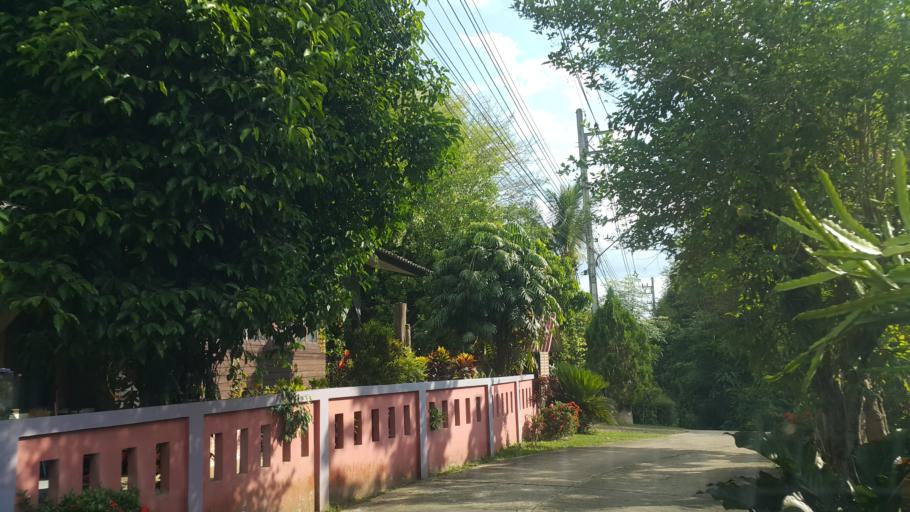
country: TH
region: Chiang Mai
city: Mae On
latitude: 18.7976
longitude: 99.2605
